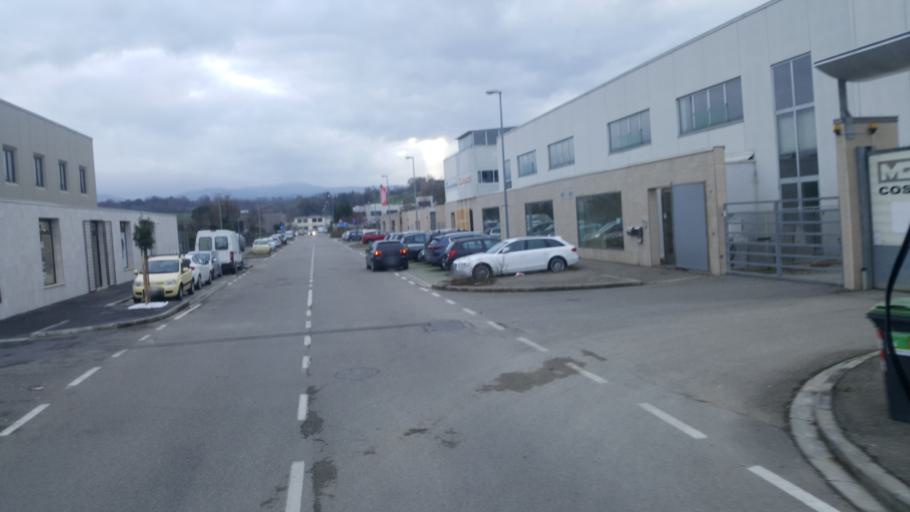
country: IT
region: Tuscany
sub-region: Province of Arezzo
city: Montevarchi
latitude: 43.5401
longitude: 11.5607
